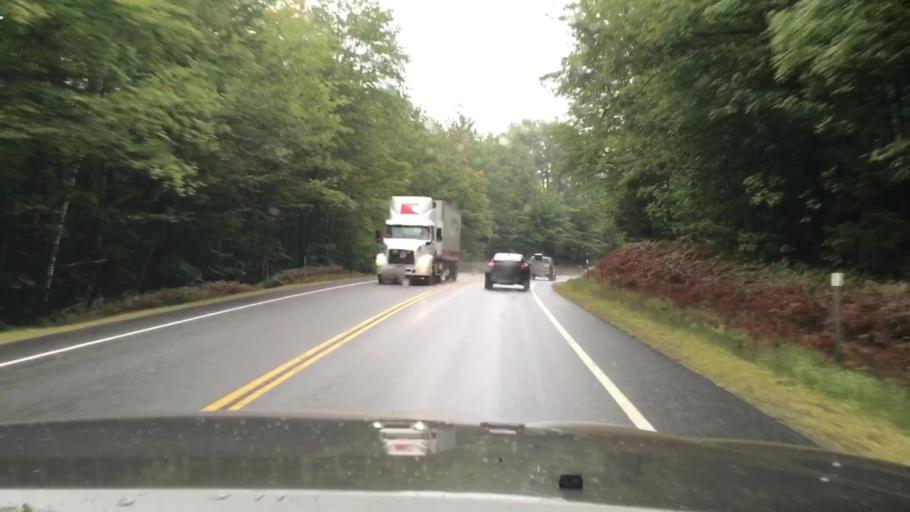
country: US
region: New Hampshire
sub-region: Cheshire County
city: Harrisville
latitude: 43.0653
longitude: -72.0672
